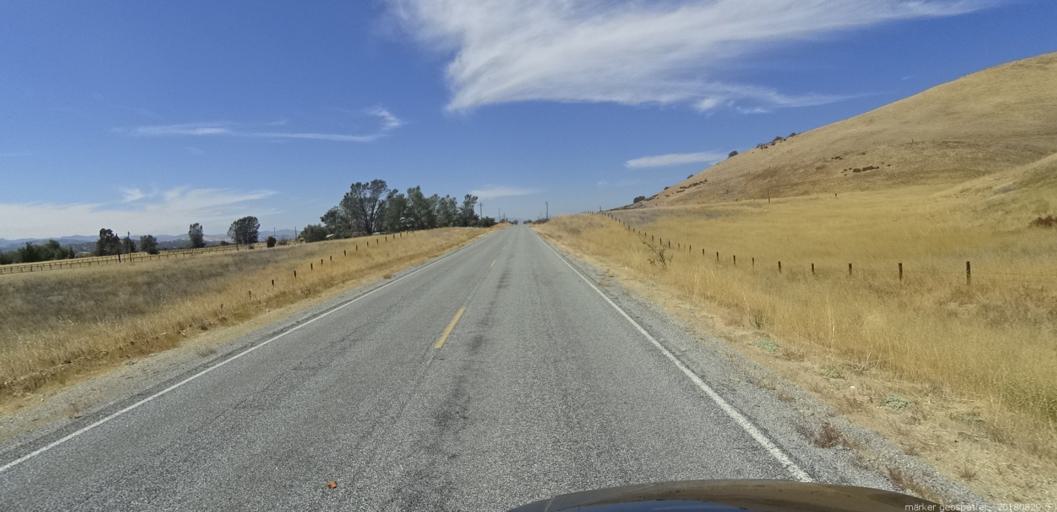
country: US
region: California
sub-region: San Luis Obispo County
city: Lake Nacimiento
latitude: 35.9128
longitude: -121.0224
